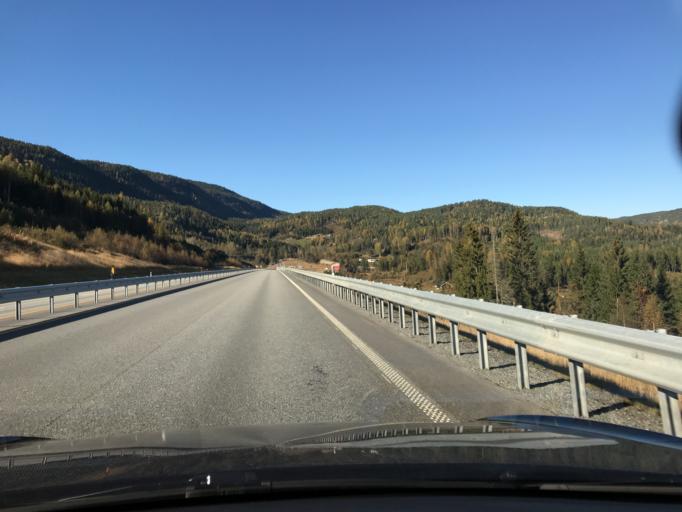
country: NO
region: Buskerud
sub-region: Krodsherad
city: Noresund
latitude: 60.2824
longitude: 9.7571
